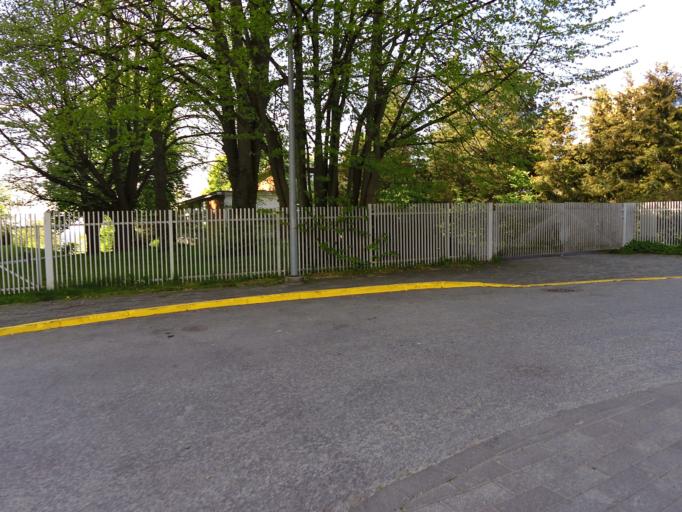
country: EE
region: Harju
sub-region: Tallinna linn
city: Tallinn
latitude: 59.4477
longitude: 24.8068
